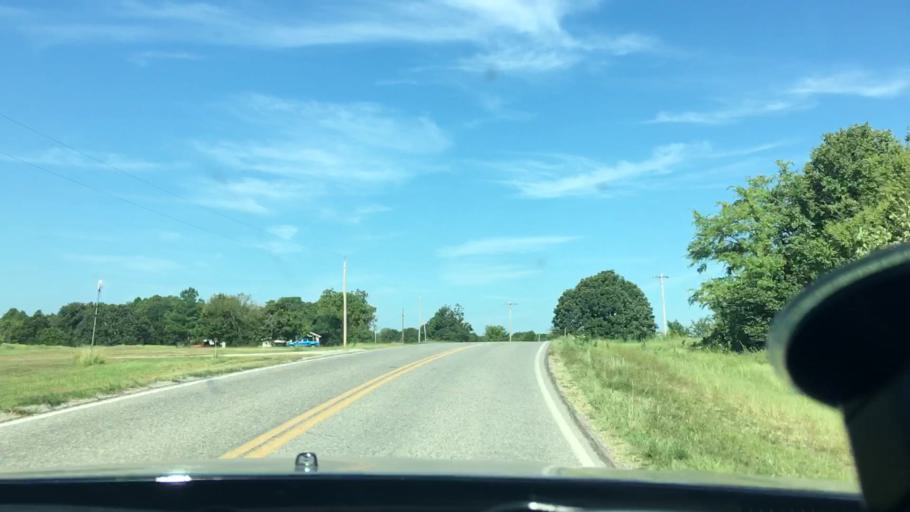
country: US
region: Oklahoma
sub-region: Johnston County
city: Tishomingo
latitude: 34.2736
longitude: -96.4519
